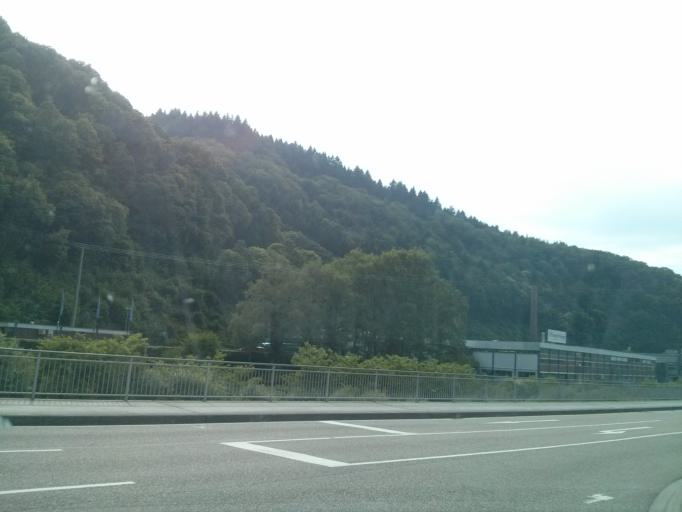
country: DE
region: Baden-Wuerttemberg
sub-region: Karlsruhe Region
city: Weisenbach
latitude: 48.7343
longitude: 8.3505
